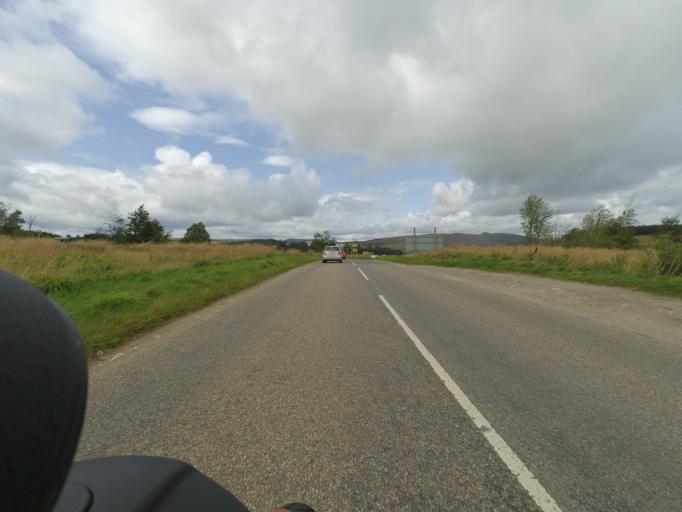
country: GB
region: Scotland
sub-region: Highland
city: Grantown on Spey
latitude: 57.2528
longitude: -3.3720
